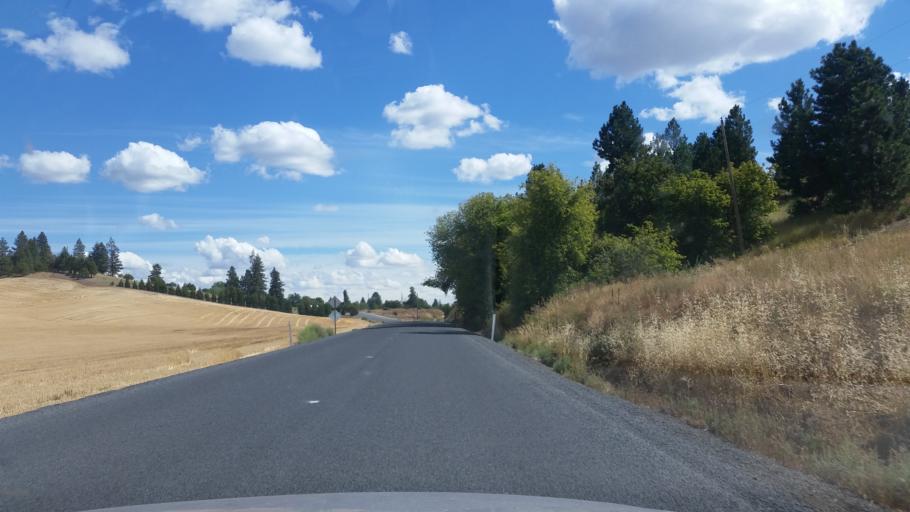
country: US
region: Washington
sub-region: Spokane County
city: Cheney
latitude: 47.4828
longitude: -117.6099
